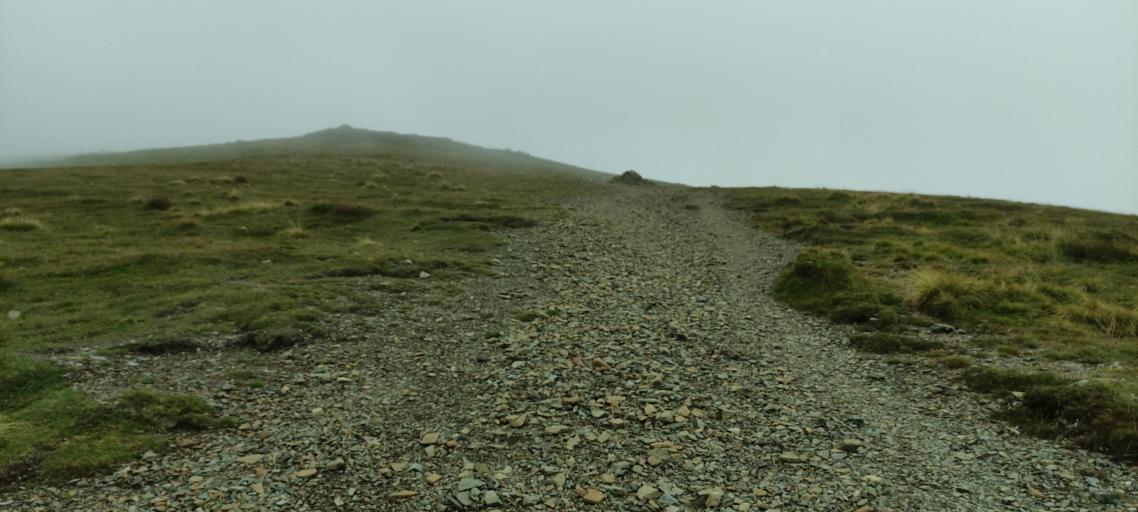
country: GB
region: England
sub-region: Cumbria
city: Ambleside
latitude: 54.5156
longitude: -2.9744
